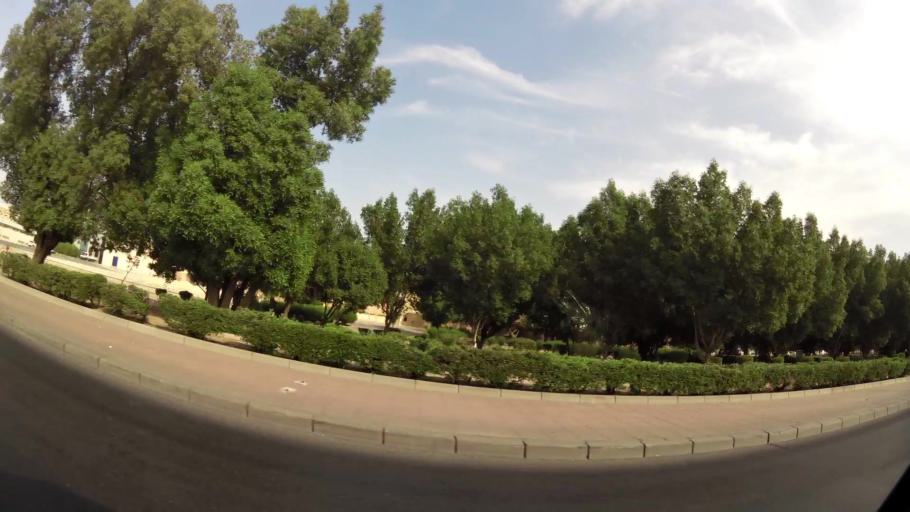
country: KW
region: Al Farwaniyah
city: Al Farwaniyah
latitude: 29.3086
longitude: 47.9626
